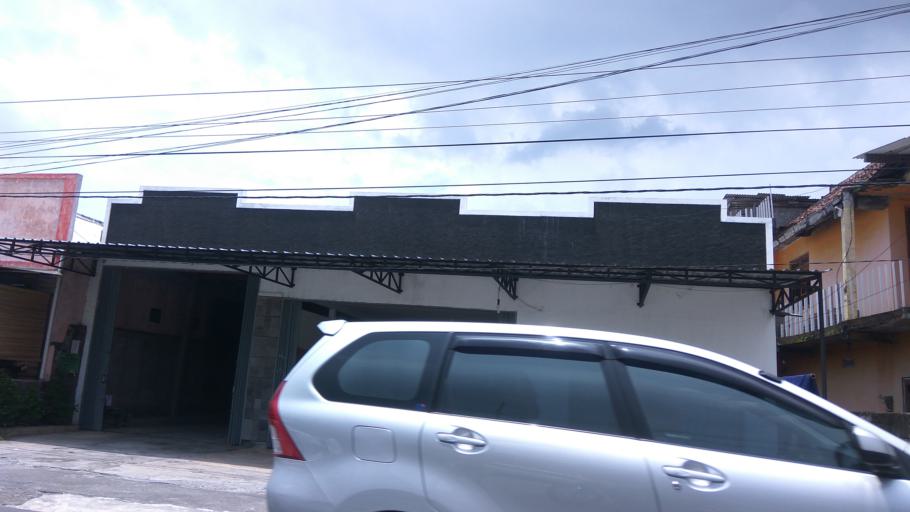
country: ID
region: Daerah Istimewa Yogyakarta
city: Melati
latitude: -7.7281
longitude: 110.3800
